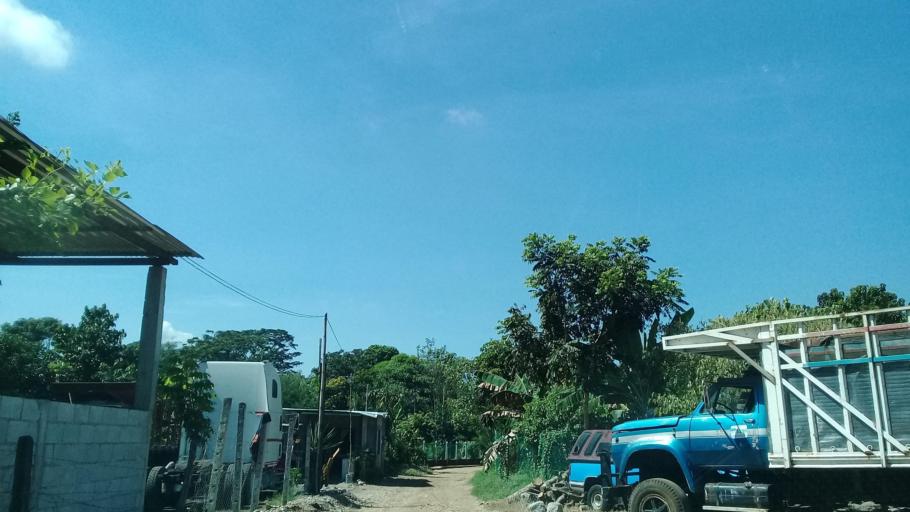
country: MX
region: Veracruz
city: Amatlan de los Reyes
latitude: 18.8569
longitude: -96.9209
